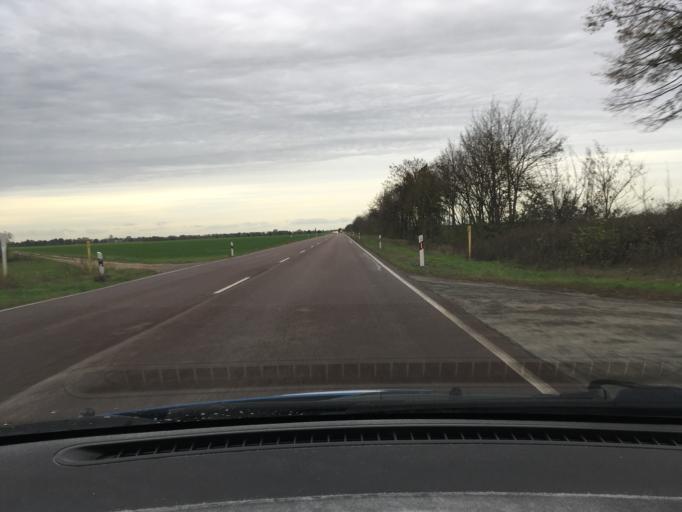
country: DE
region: Saxony-Anhalt
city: Zerbst
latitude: 51.9796
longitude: 12.0592
